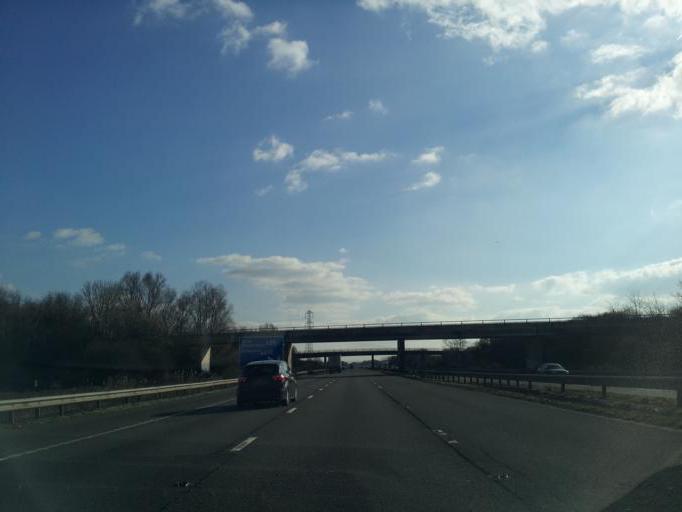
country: GB
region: England
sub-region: Somerset
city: Puriton
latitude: 51.1853
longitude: -2.9743
